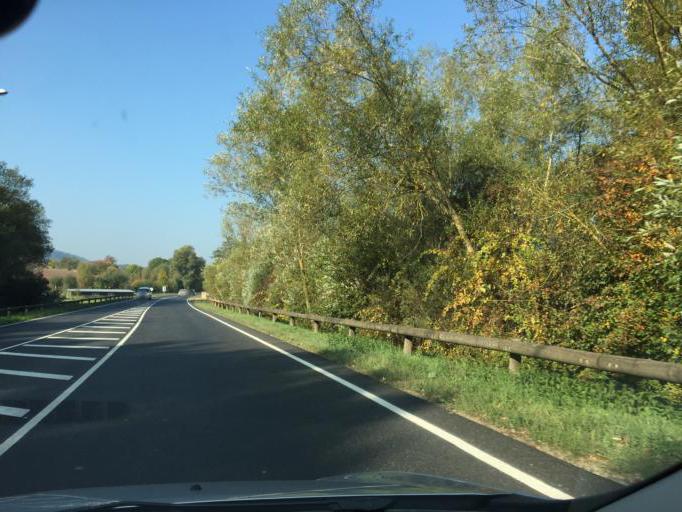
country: LU
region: Grevenmacher
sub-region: Canton de Remich
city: Bous
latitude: 49.5533
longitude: 6.3324
